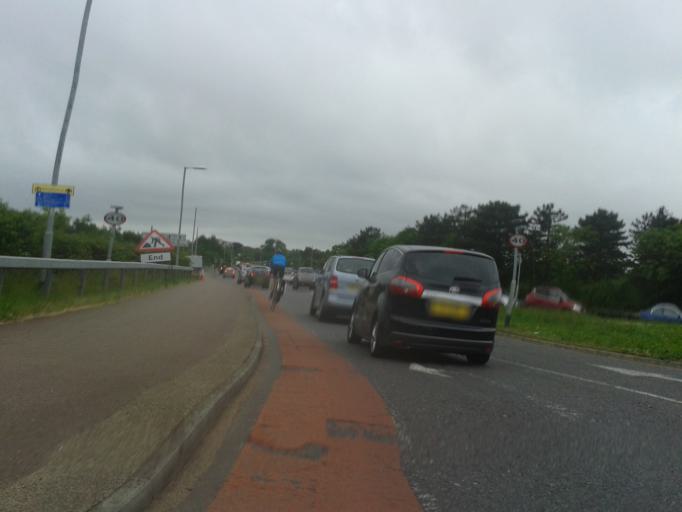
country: GB
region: England
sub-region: Cambridgeshire
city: Histon
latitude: 52.2345
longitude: 0.1134
